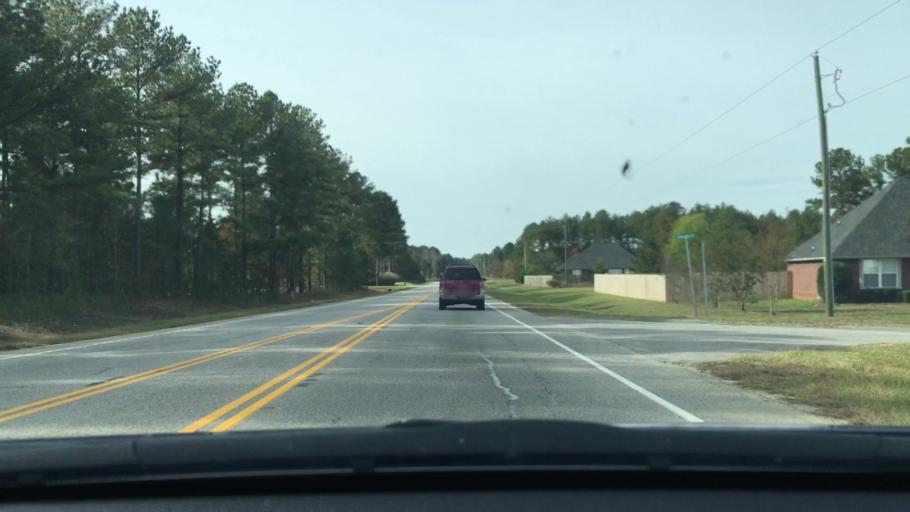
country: US
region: South Carolina
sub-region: Sumter County
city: Cherryvale
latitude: 33.9392
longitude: -80.4771
